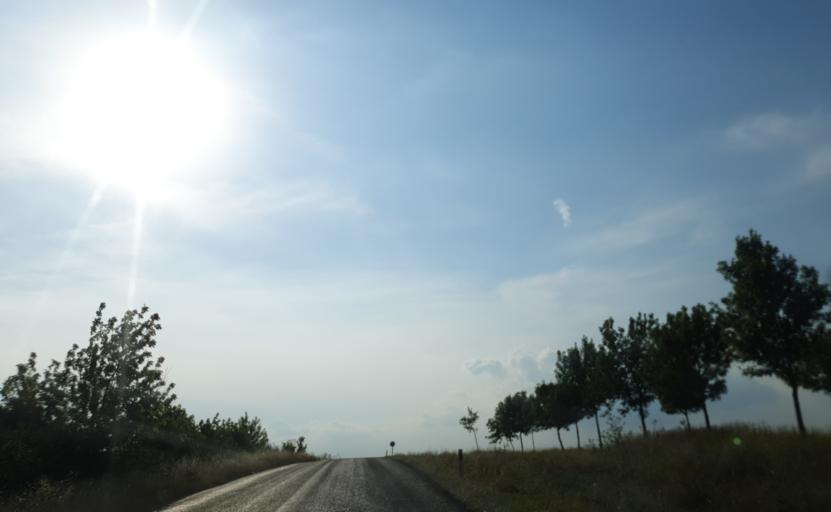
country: TR
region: Tekirdag
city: Muratli
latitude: 41.2045
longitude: 27.4631
